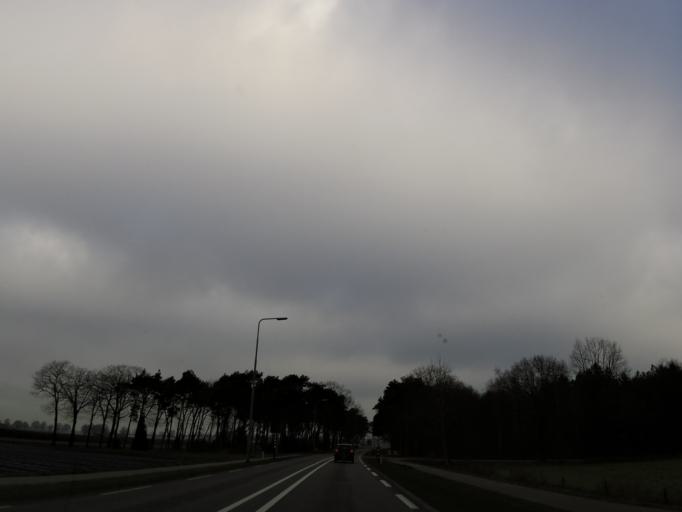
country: NL
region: Limburg
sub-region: Gemeente Venray
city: Venray
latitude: 51.4391
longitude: 5.9492
